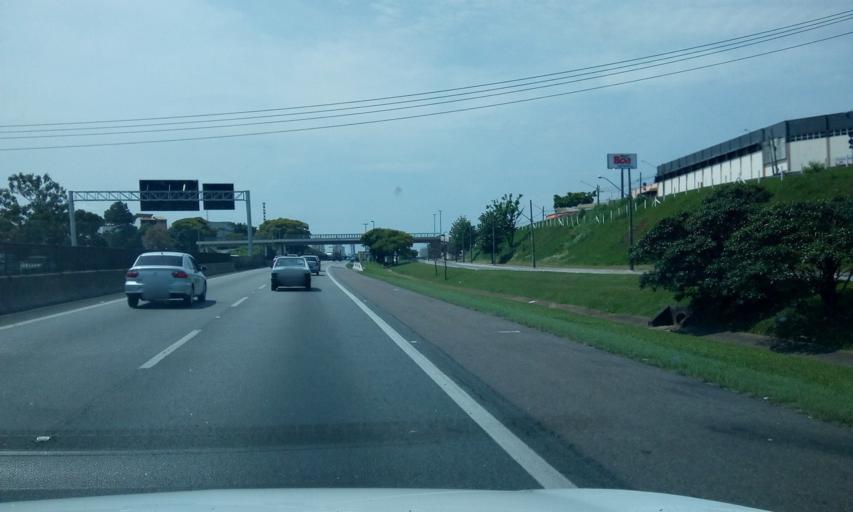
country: BR
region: Sao Paulo
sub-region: Jundiai
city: Jundiai
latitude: -23.1790
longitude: -46.9140
